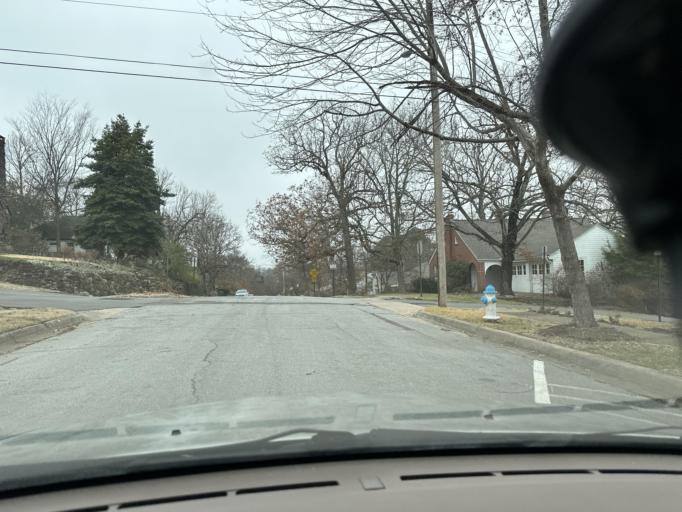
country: US
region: Arkansas
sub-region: Washington County
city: Fayetteville
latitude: 36.0709
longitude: -94.1615
